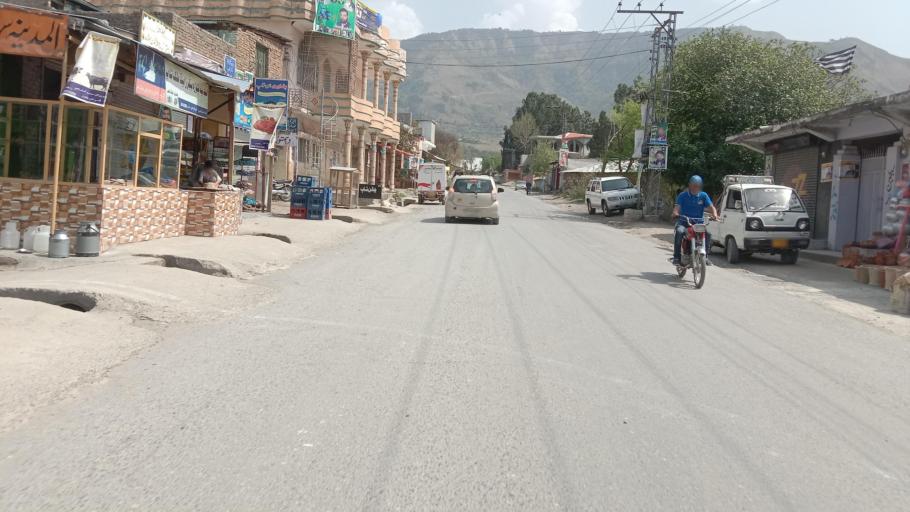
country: PK
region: Khyber Pakhtunkhwa
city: Abbottabad
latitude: 34.1393
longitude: 73.2753
